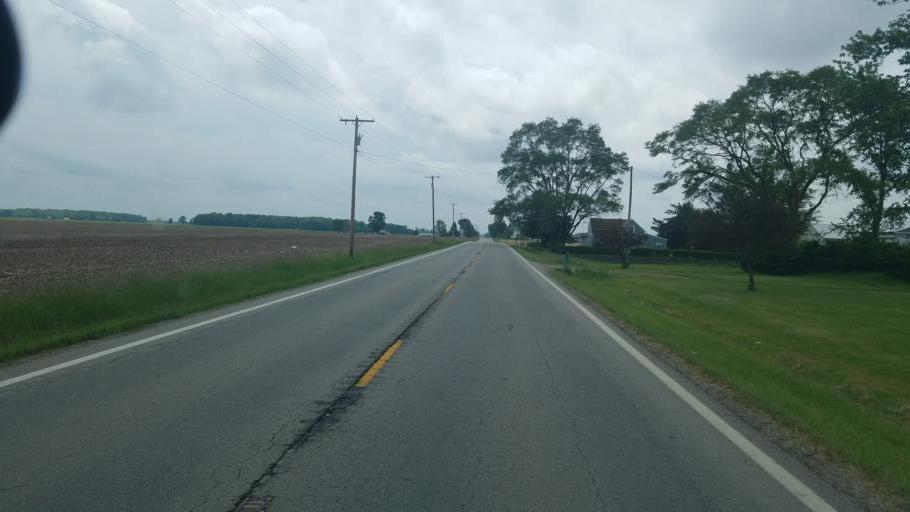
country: US
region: Ohio
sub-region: Marion County
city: Prospect
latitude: 40.4386
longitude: -83.2318
